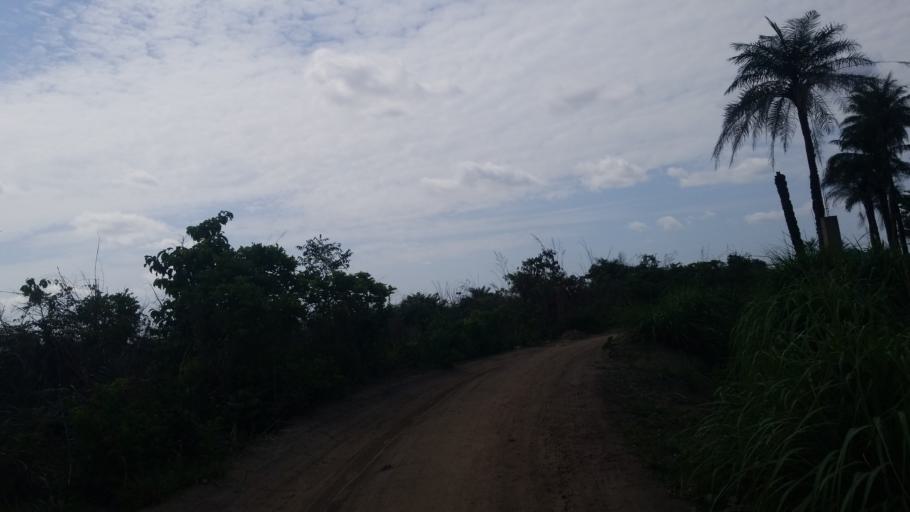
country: SL
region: Western Area
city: Waterloo
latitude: 8.3255
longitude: -13.0252
